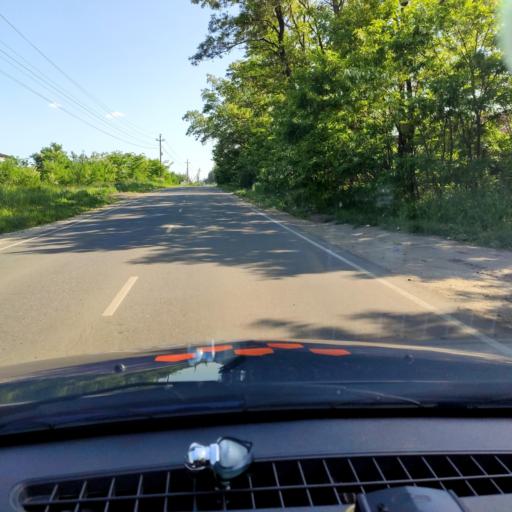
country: RU
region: Voronezj
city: Podgornoye
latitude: 51.8189
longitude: 39.1421
